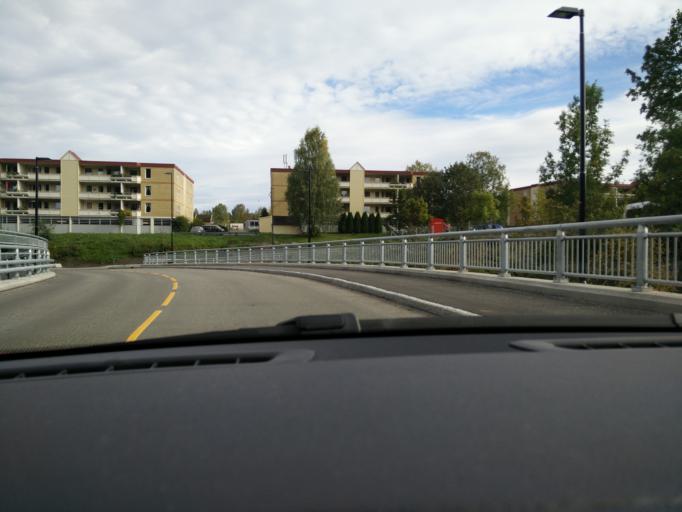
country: NO
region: Akershus
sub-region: Asker
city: Blakstad
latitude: 59.7855
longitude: 10.4303
